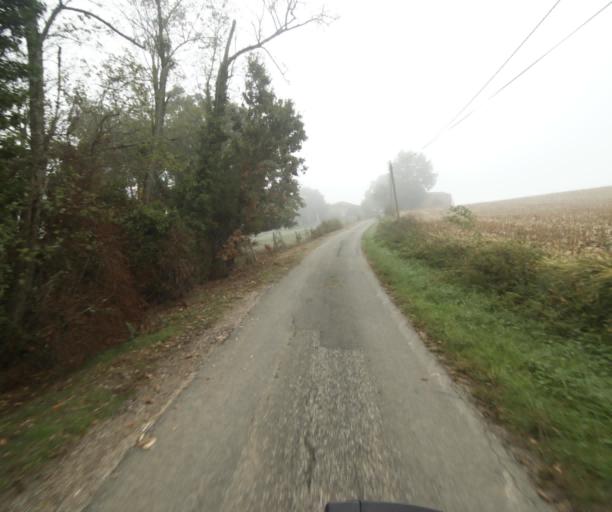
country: FR
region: Midi-Pyrenees
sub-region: Departement du Tarn-et-Garonne
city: Nohic
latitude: 43.9117
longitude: 1.4682
